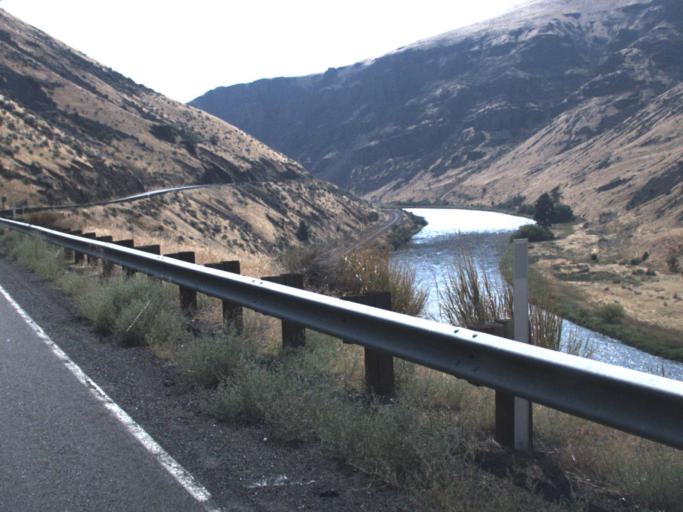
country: US
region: Washington
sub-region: Yakima County
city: Selah
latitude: 46.7405
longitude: -120.4474
